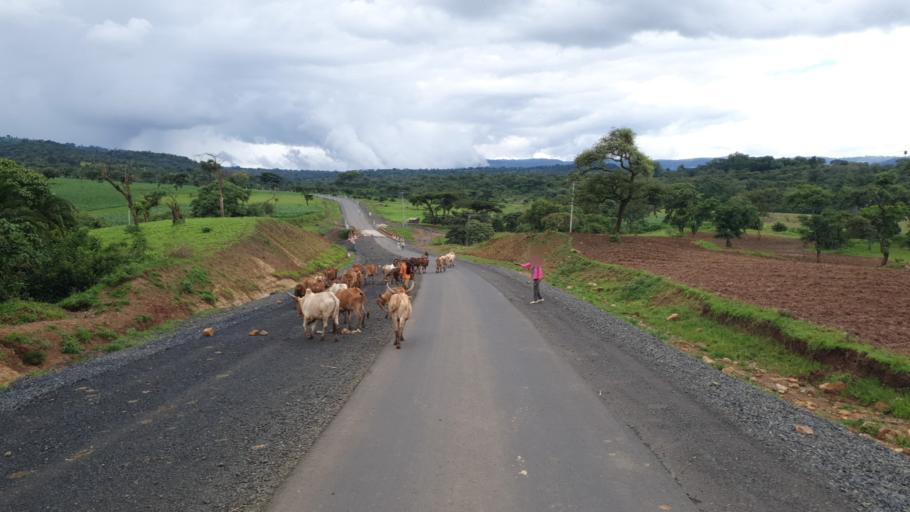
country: ET
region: Oromiya
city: Shambu
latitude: 10.0863
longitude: 36.8955
